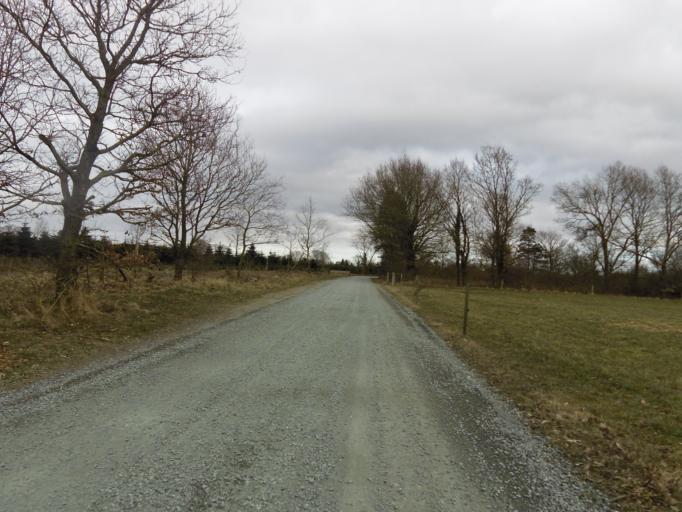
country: DK
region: South Denmark
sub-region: Tonder Kommune
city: Toftlund
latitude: 55.2112
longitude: 9.1729
